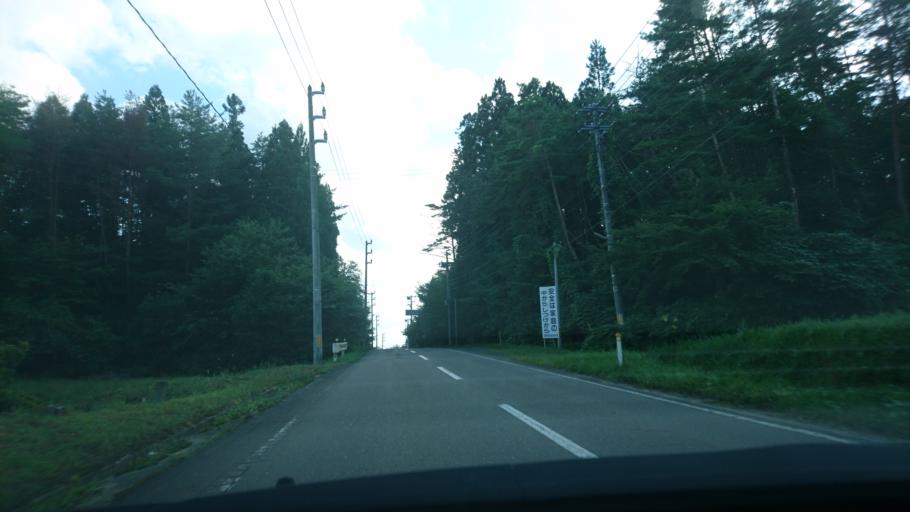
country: JP
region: Iwate
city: Ichinoseki
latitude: 39.0100
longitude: 141.2864
